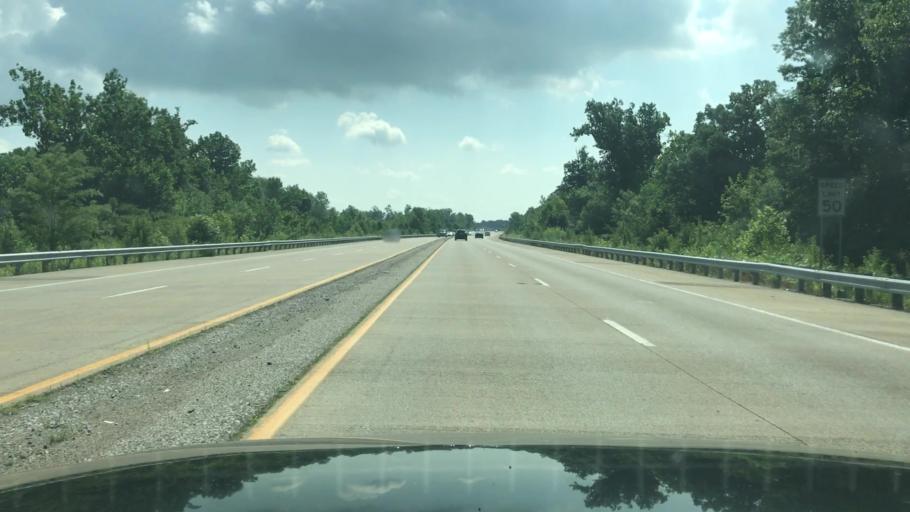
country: US
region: Indiana
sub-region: Vanderburgh County
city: Melody Hill
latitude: 38.0131
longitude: -87.5037
